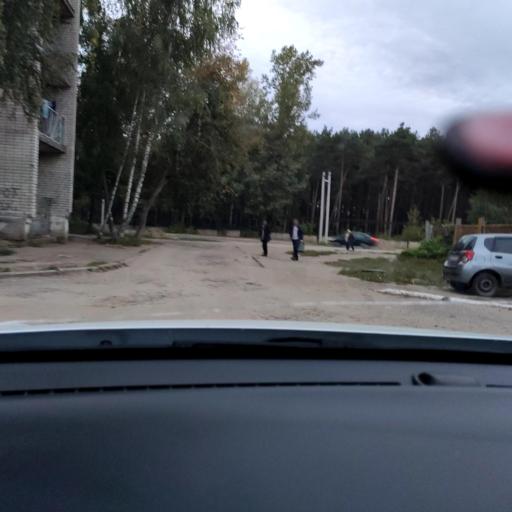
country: RU
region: Mariy-El
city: Volzhsk
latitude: 55.8670
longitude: 48.3442
